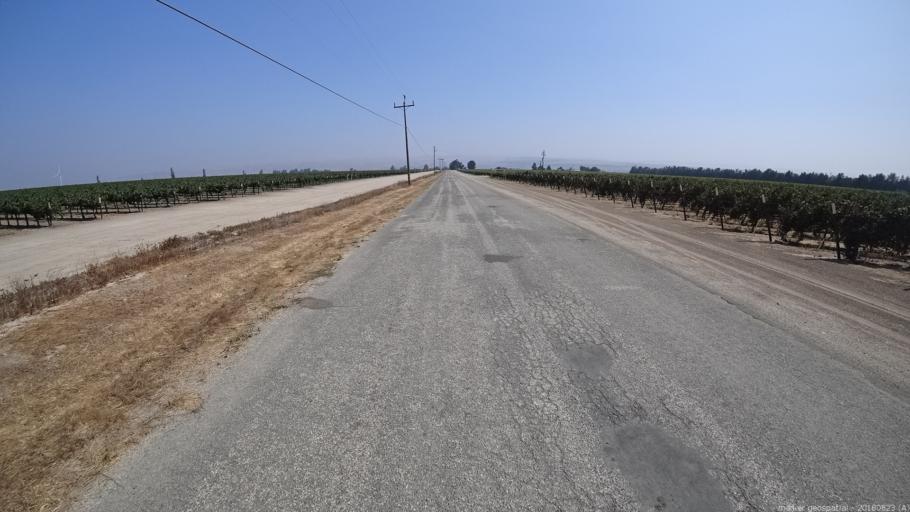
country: US
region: California
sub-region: Monterey County
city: King City
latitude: 36.2546
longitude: -121.1927
